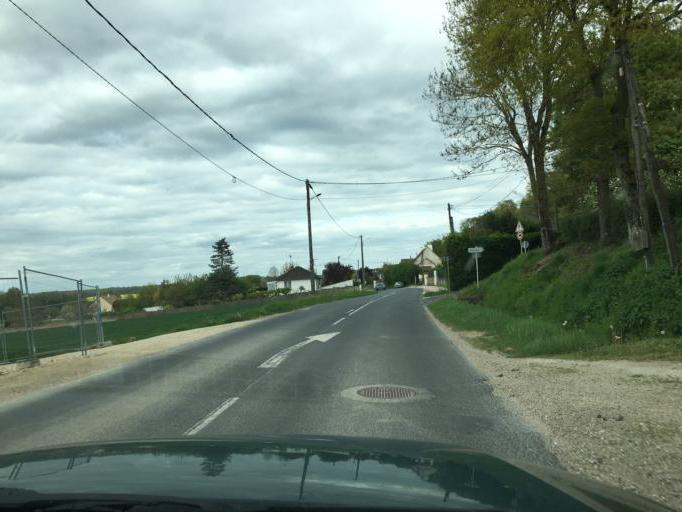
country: FR
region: Centre
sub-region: Departement du Loir-et-Cher
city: Saint-Ouen
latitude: 47.7939
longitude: 1.0897
